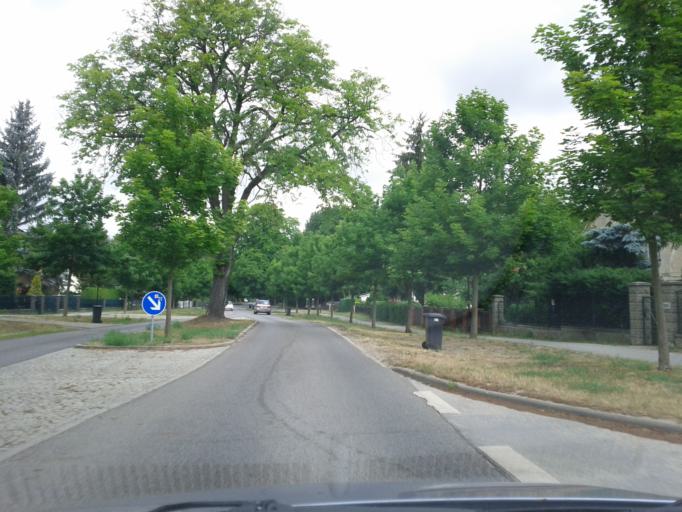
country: DE
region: Brandenburg
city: Woltersdorf
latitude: 52.4586
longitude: 13.7338
